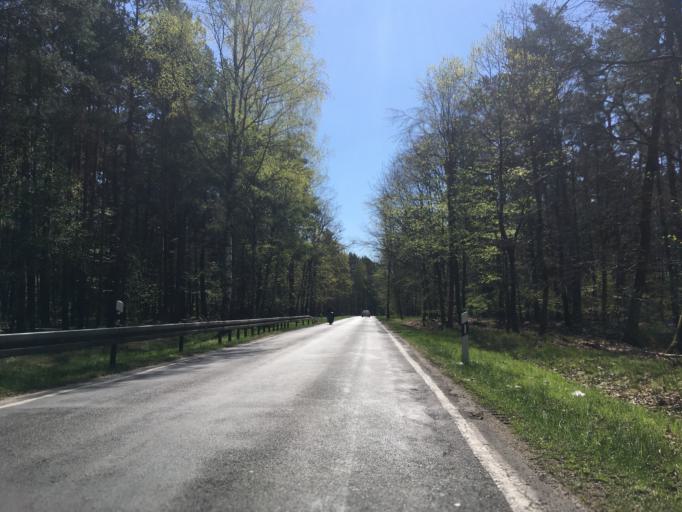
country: DE
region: Brandenburg
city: Bernau bei Berlin
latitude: 52.7141
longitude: 13.5774
